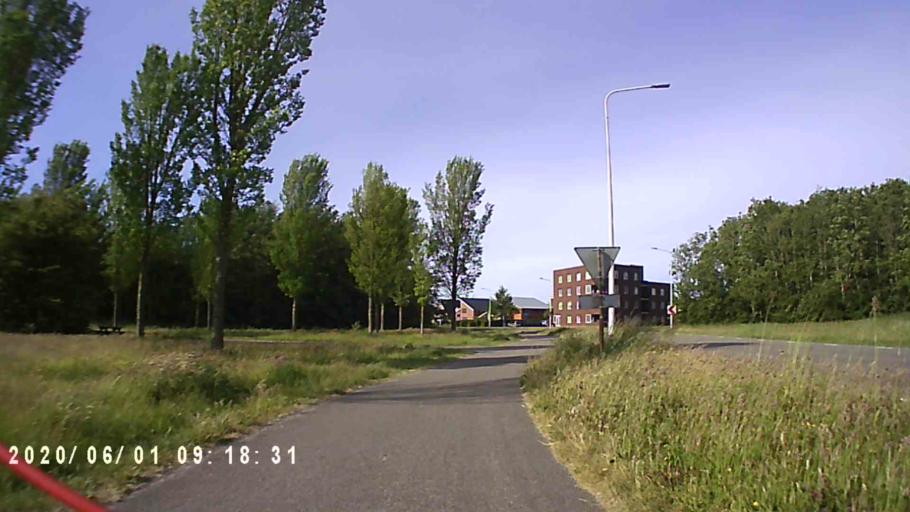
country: NL
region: Friesland
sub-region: Gemeente Leeuwarderadeel
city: Stiens
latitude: 53.2696
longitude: 5.7607
